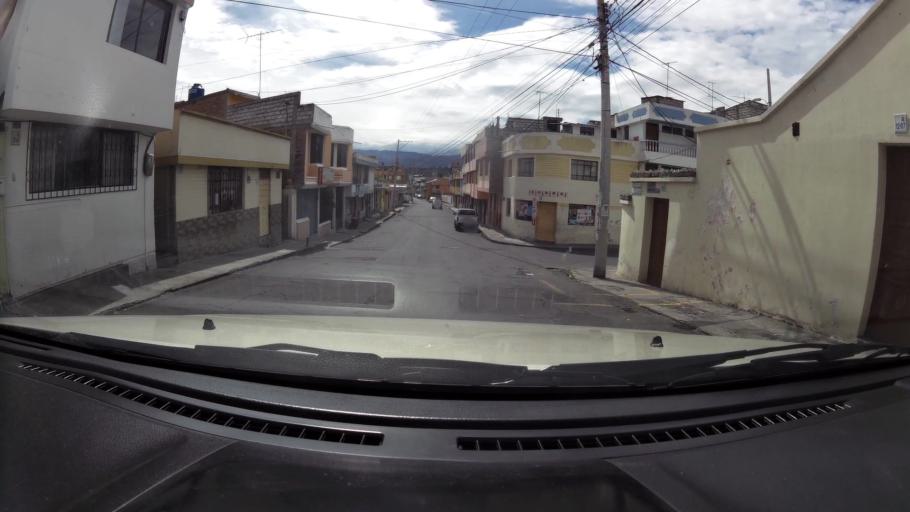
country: EC
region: Cotopaxi
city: Latacunga
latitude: -0.9241
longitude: -78.6220
